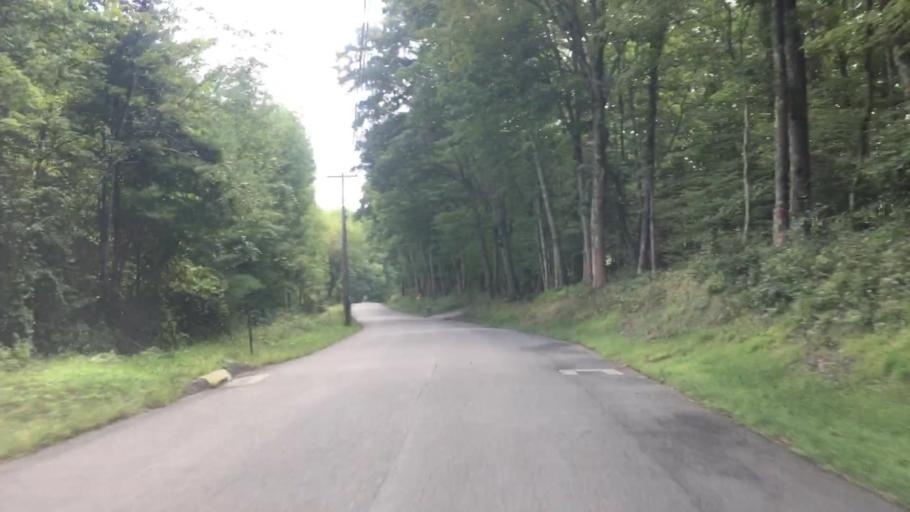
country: US
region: Connecticut
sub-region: Tolland County
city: Stafford Springs
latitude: 41.9199
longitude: -72.2283
